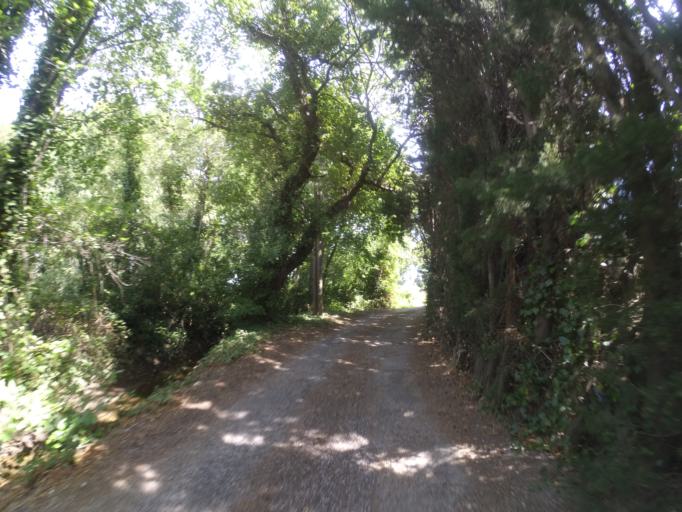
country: FR
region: Languedoc-Roussillon
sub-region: Departement des Pyrenees-Orientales
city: Ille-sur-Tet
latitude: 42.6811
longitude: 2.6434
